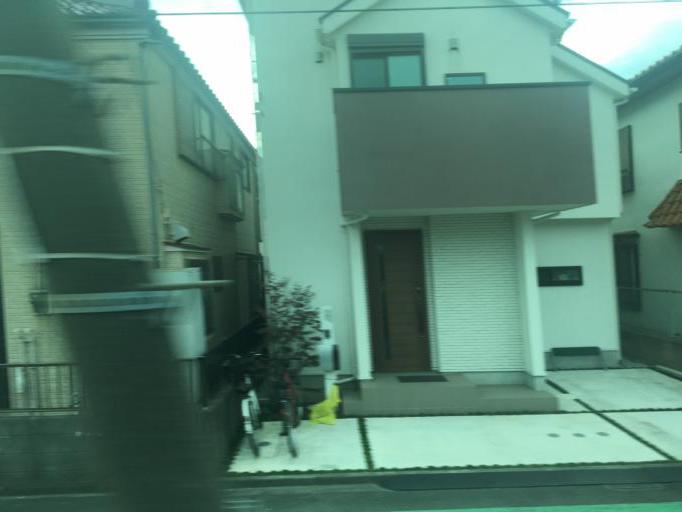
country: JP
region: Tokyo
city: Kokubunji
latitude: 35.6724
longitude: 139.4548
